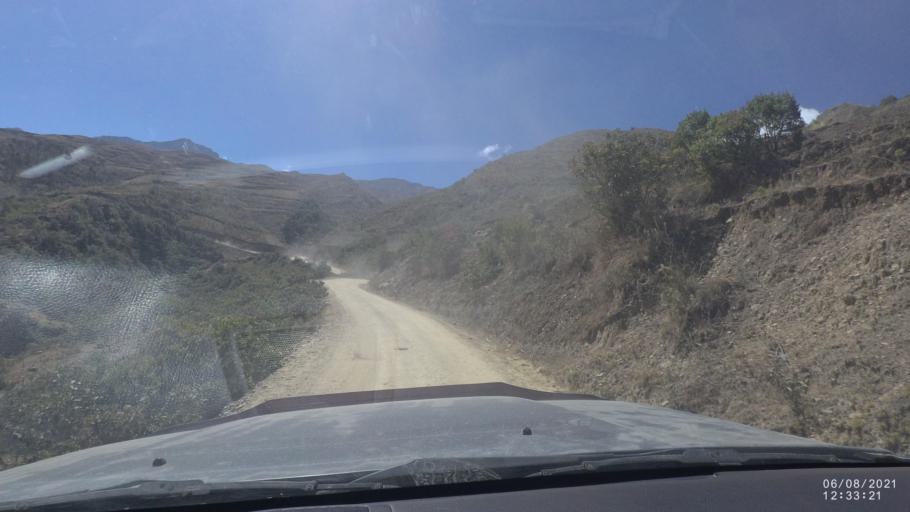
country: BO
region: Cochabamba
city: Colchani
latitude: -16.7799
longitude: -66.6451
